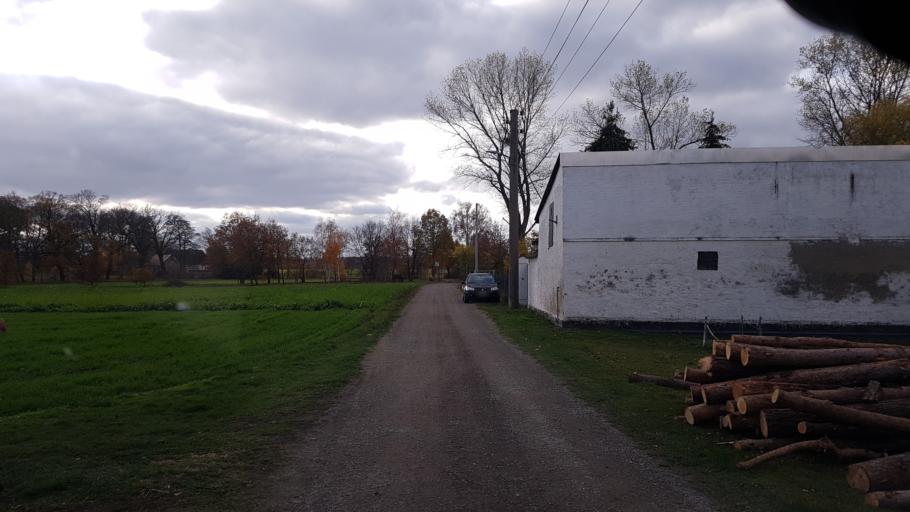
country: DE
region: Brandenburg
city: Sallgast
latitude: 51.6030
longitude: 13.8572
